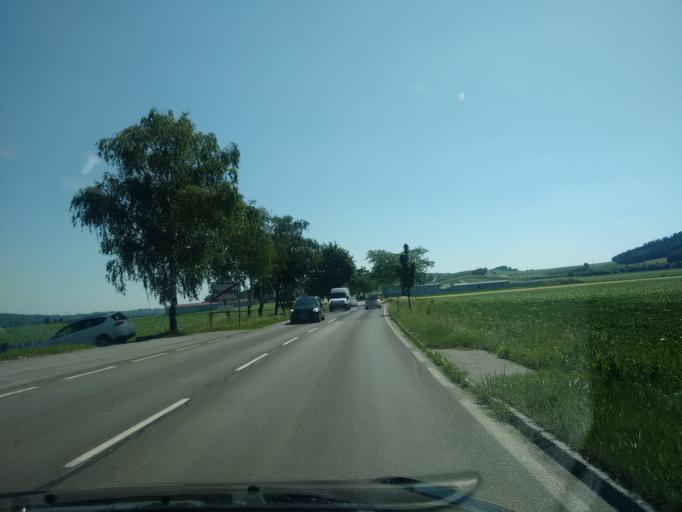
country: AT
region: Lower Austria
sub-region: Politischer Bezirk Sankt Polten
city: Kapelln
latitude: 48.2605
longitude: 15.8048
